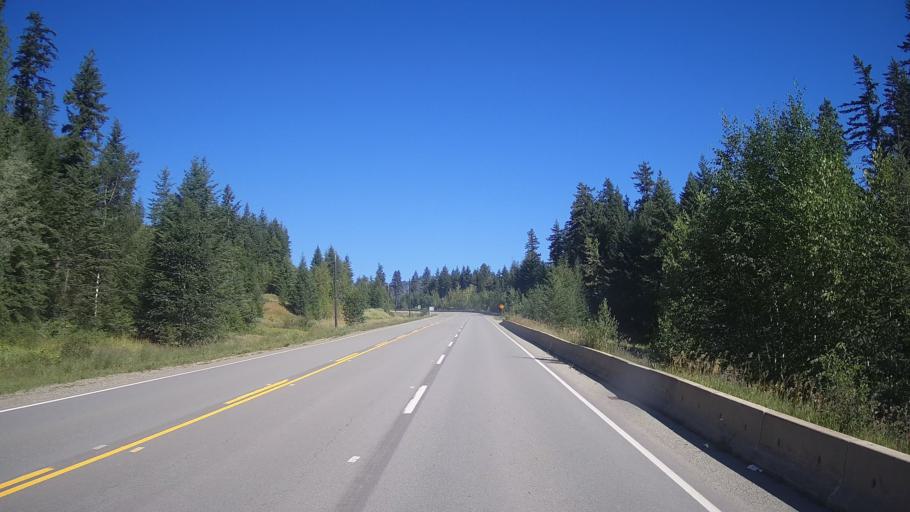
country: CA
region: British Columbia
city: Kamloops
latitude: 51.4637
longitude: -120.2320
